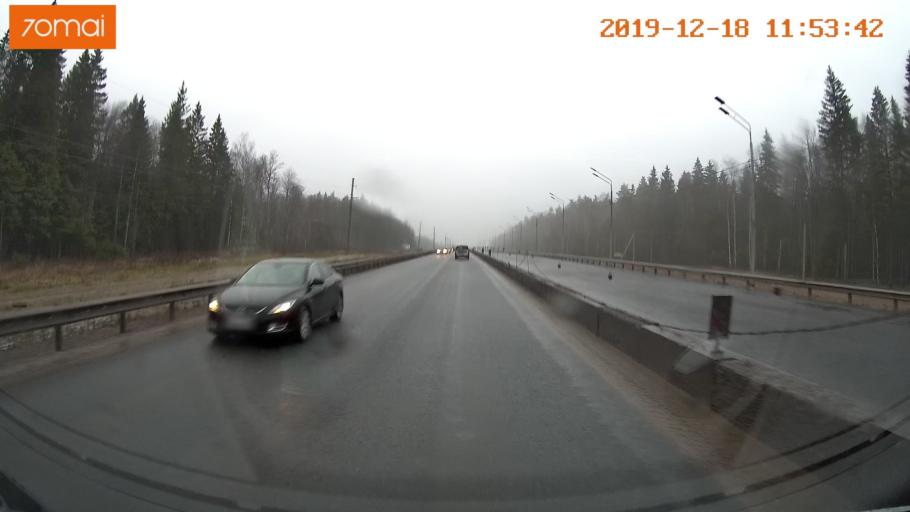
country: RU
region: Moskovskaya
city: Yershovo
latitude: 55.8072
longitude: 36.9195
